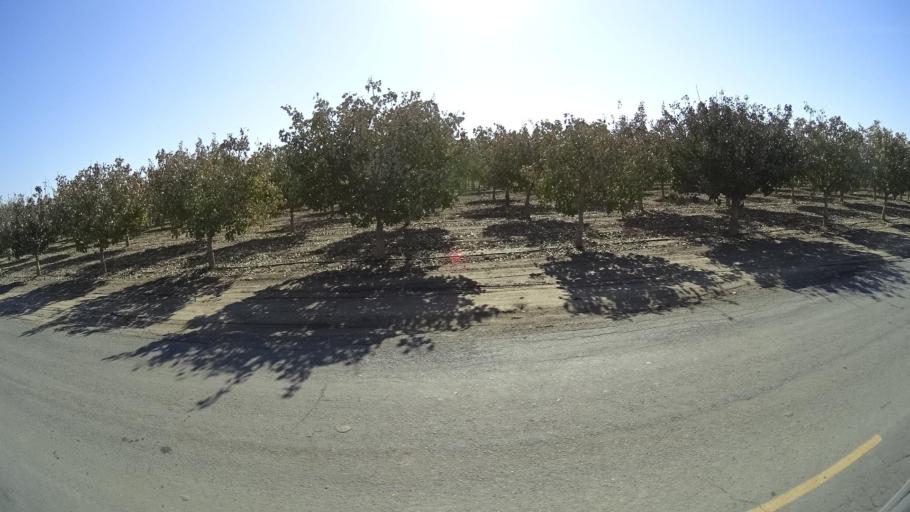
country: US
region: California
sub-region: Kern County
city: McFarland
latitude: 35.7034
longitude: -119.2200
